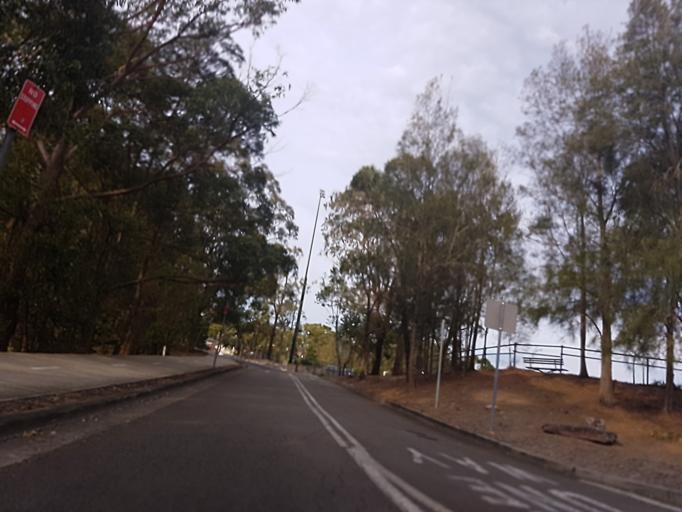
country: AU
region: New South Wales
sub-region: North Sydney
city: St Leonards
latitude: -33.8122
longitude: 151.2019
